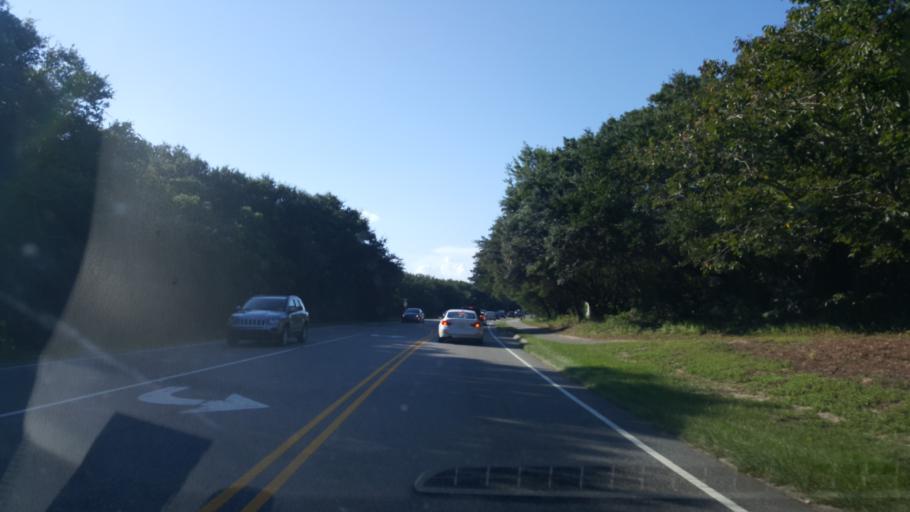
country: US
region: North Carolina
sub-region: Dare County
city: Southern Shores
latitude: 36.1444
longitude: -75.7399
